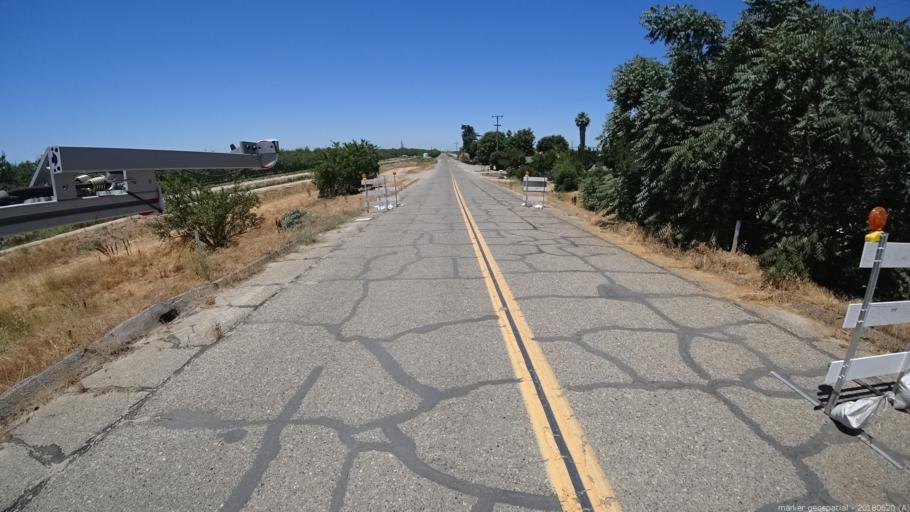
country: US
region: California
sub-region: Fresno County
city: Biola
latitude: 36.8658
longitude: -119.9626
